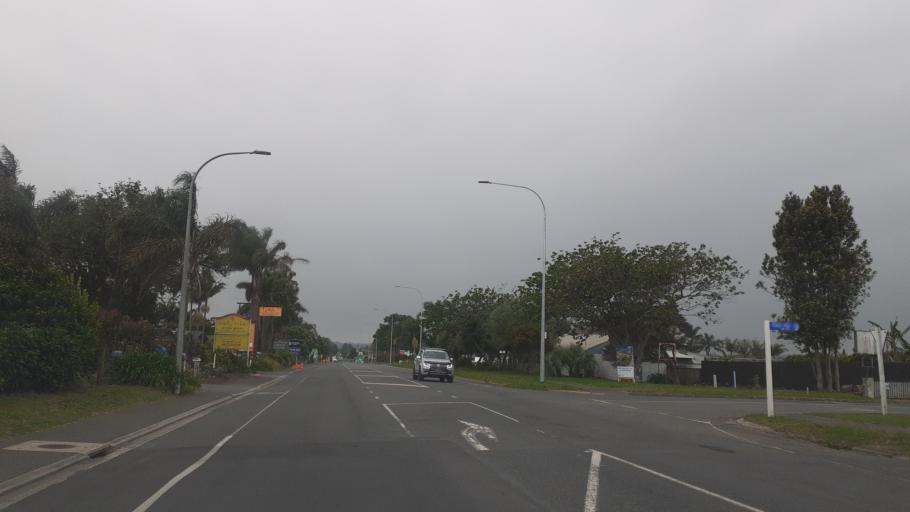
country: NZ
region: Northland
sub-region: Far North District
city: Kerikeri
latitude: -35.2340
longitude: 173.9432
